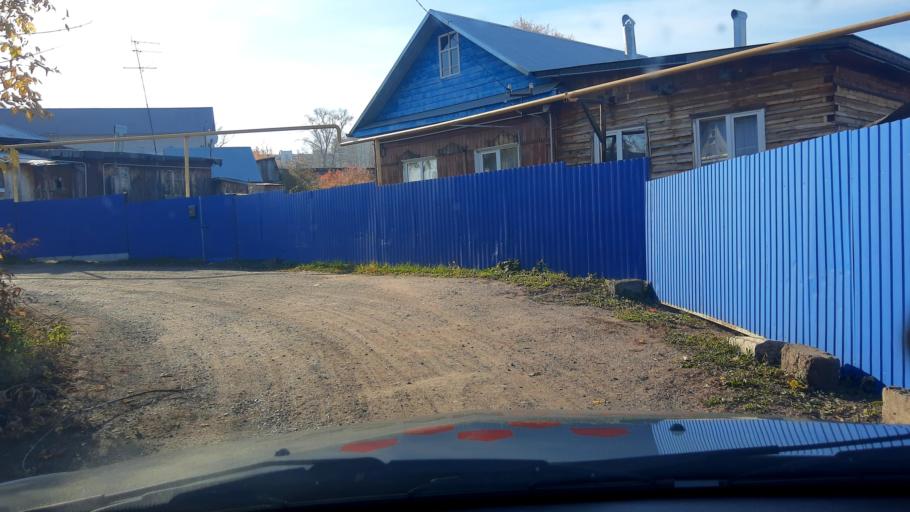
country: RU
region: Bashkortostan
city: Ufa
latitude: 54.8292
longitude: 56.0726
